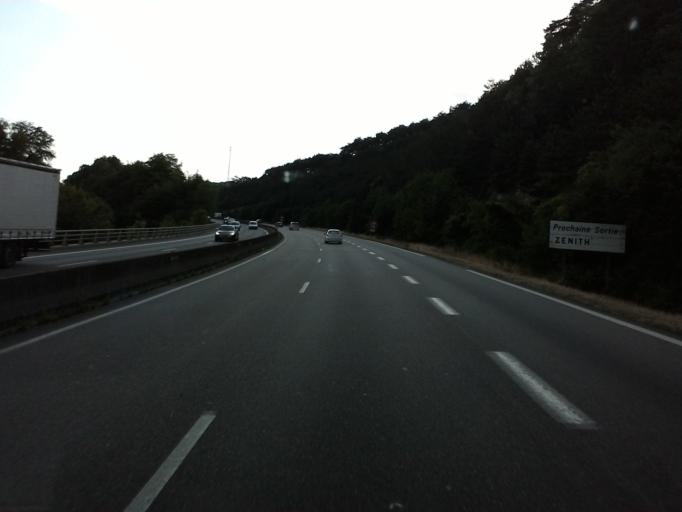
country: FR
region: Lorraine
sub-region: Departement de Meurthe-et-Moselle
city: Maxeville
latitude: 48.7137
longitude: 6.1515
